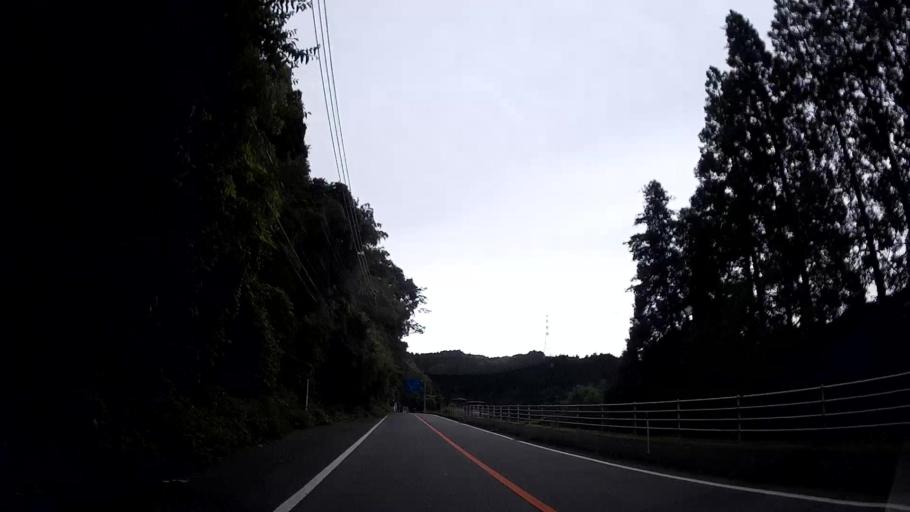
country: JP
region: Kumamoto
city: Kikuchi
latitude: 33.0156
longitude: 130.8901
